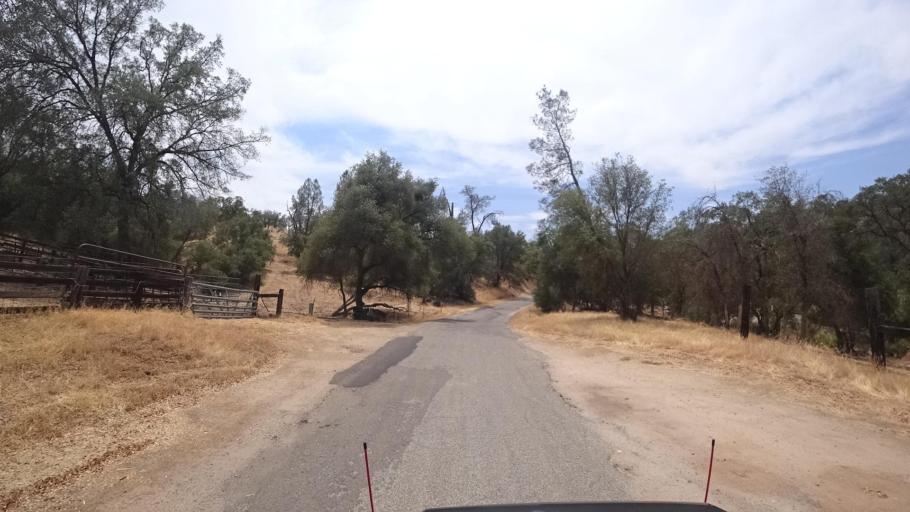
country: US
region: California
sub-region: Madera County
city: Yosemite Lakes
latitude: 37.2830
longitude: -119.8705
